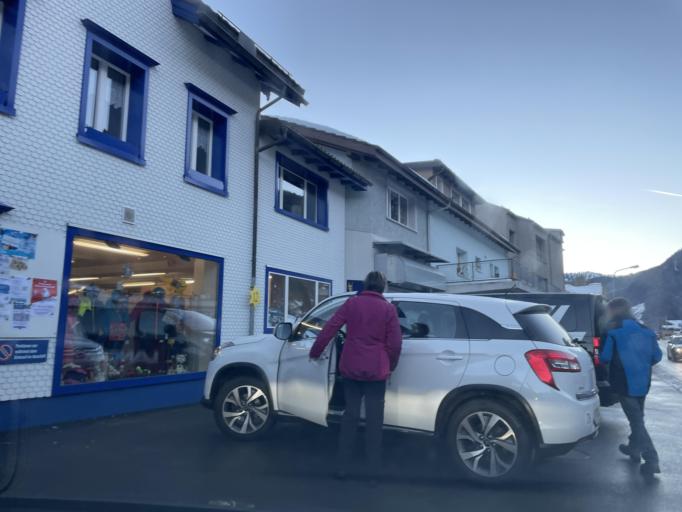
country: CH
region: Saint Gallen
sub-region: Wahlkreis Toggenburg
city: Wildhaus
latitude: 47.1924
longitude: 9.2821
